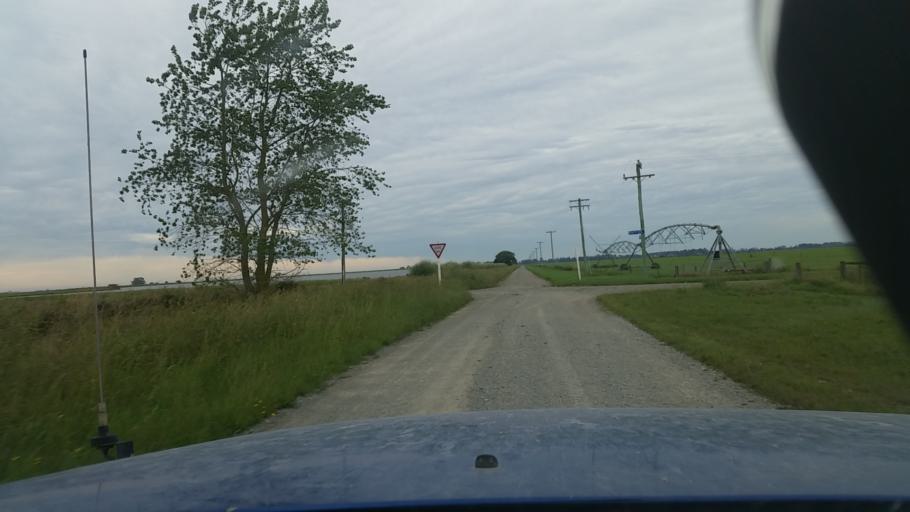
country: NZ
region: Canterbury
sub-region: Ashburton District
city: Tinwald
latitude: -43.9377
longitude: 171.5626
